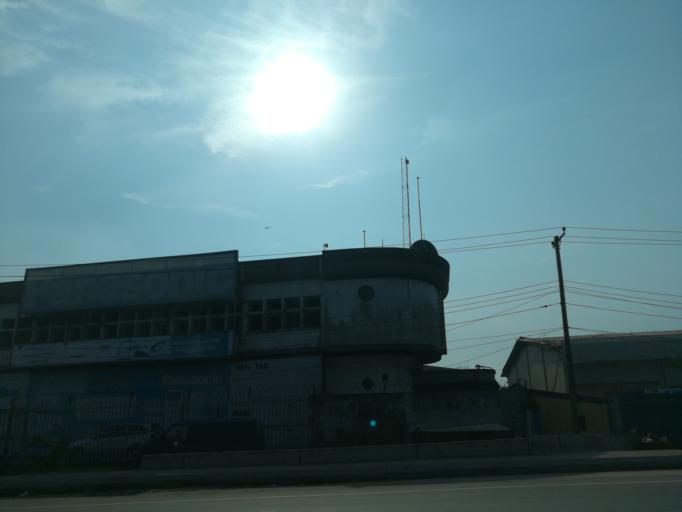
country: NG
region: Rivers
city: Port Harcourt
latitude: 4.8081
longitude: 7.0123
